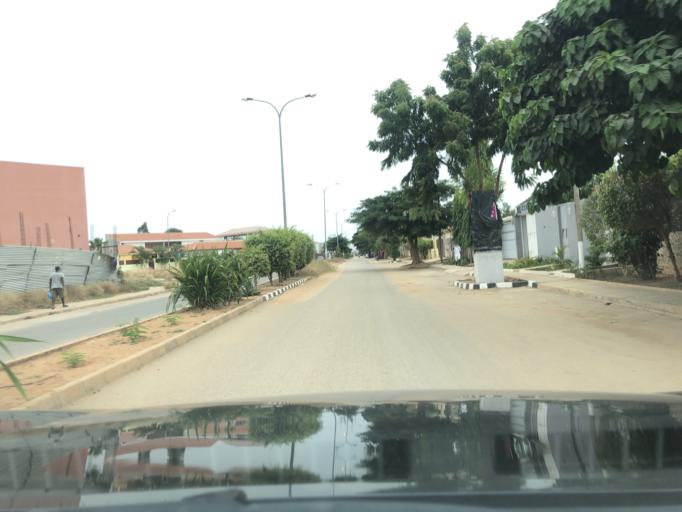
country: AO
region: Luanda
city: Luanda
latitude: -8.9348
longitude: 13.2503
